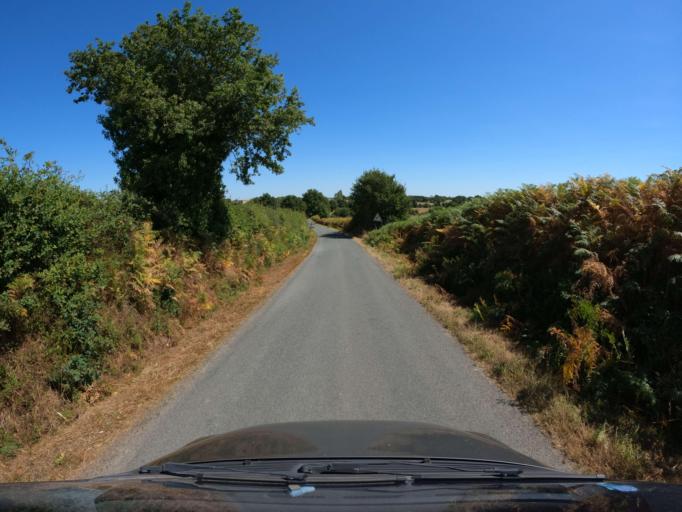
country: FR
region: Pays de la Loire
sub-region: Departement de Maine-et-Loire
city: Saint-Christophe-du-Bois
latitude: 47.0511
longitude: -0.9663
